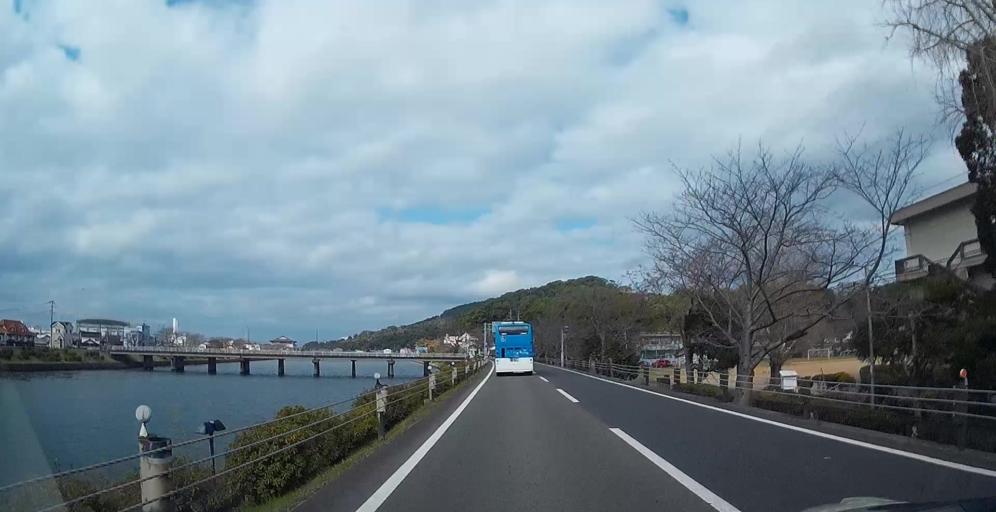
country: JP
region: Kumamoto
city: Minamata
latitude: 32.2131
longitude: 130.4070
